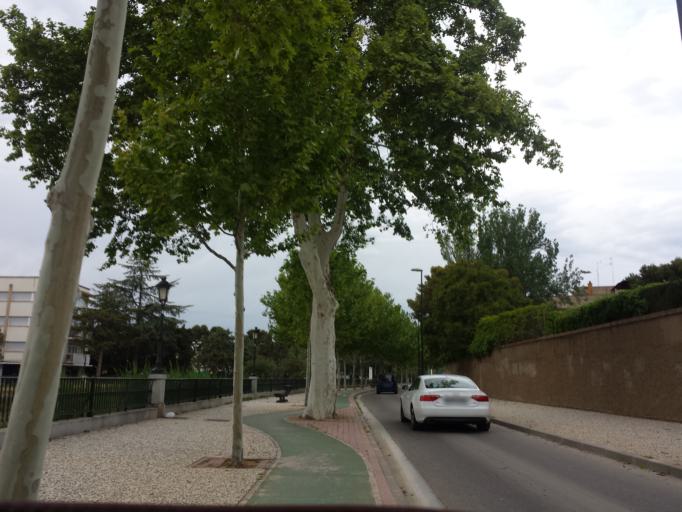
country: ES
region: Aragon
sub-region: Provincia de Zaragoza
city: Delicias
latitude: 41.6233
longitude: -0.9057
